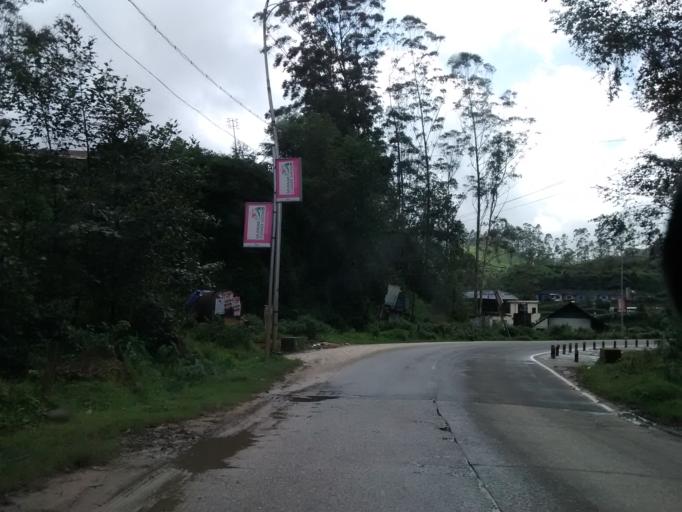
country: IN
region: Kerala
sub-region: Idukki
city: Munnar
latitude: 10.0693
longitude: 77.0613
